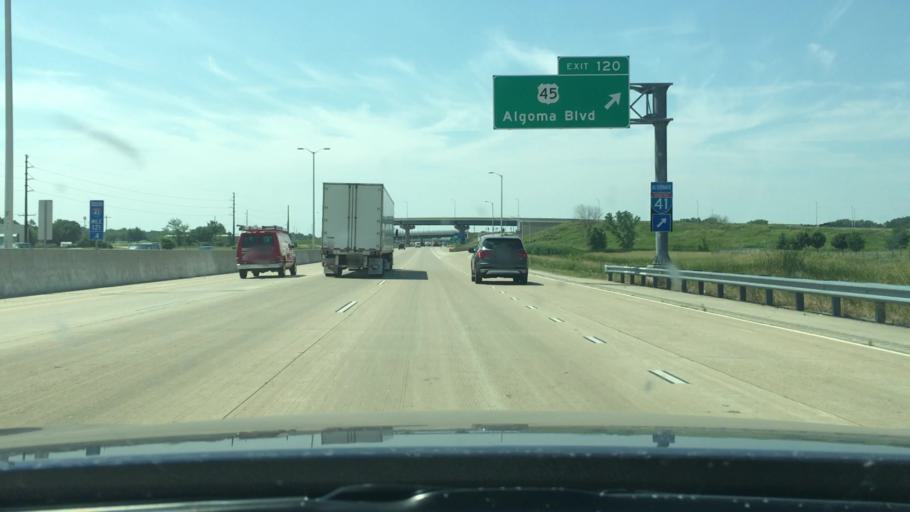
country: US
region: Wisconsin
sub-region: Winnebago County
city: Oshkosh
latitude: 44.0651
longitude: -88.5709
